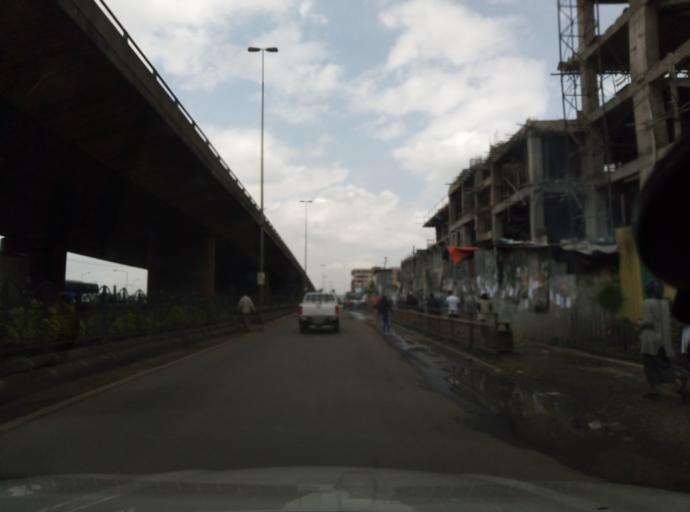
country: ET
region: Adis Abeba
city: Addis Ababa
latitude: 9.0104
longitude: 38.7206
